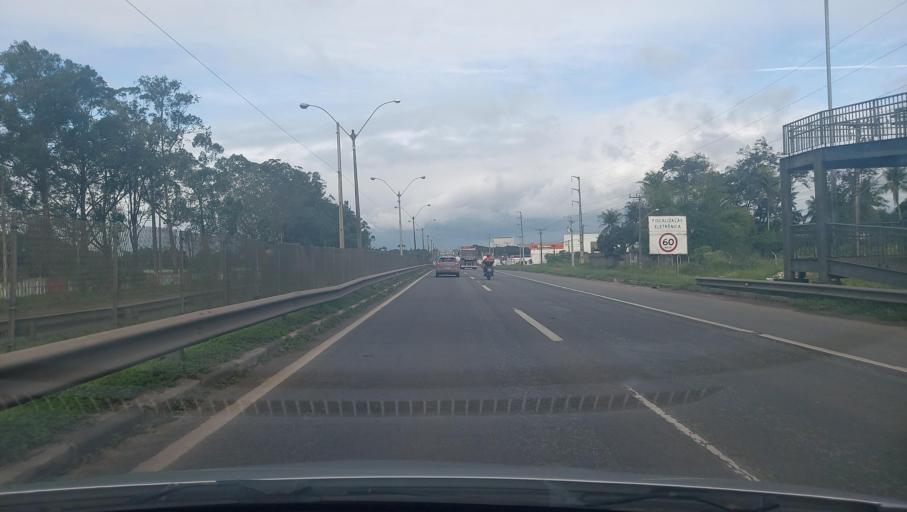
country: BR
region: Bahia
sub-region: Feira De Santana
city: Feira de Santana
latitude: -12.2958
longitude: -38.9045
